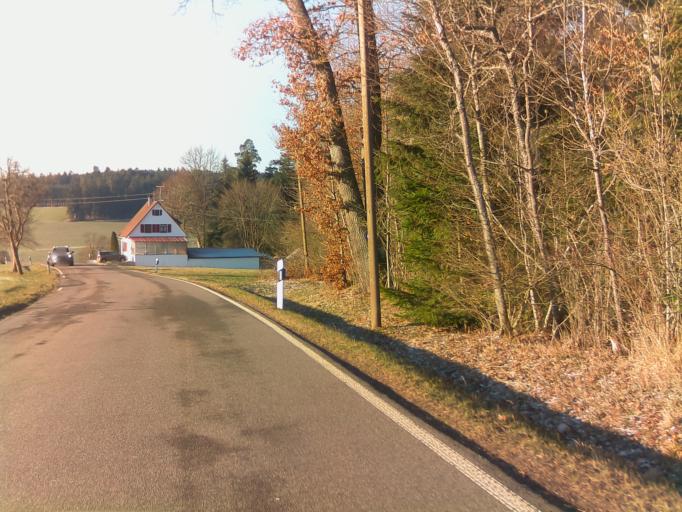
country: DE
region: Baden-Wuerttemberg
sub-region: Karlsruhe Region
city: Oberreichenbach
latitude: 48.7392
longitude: 8.6616
